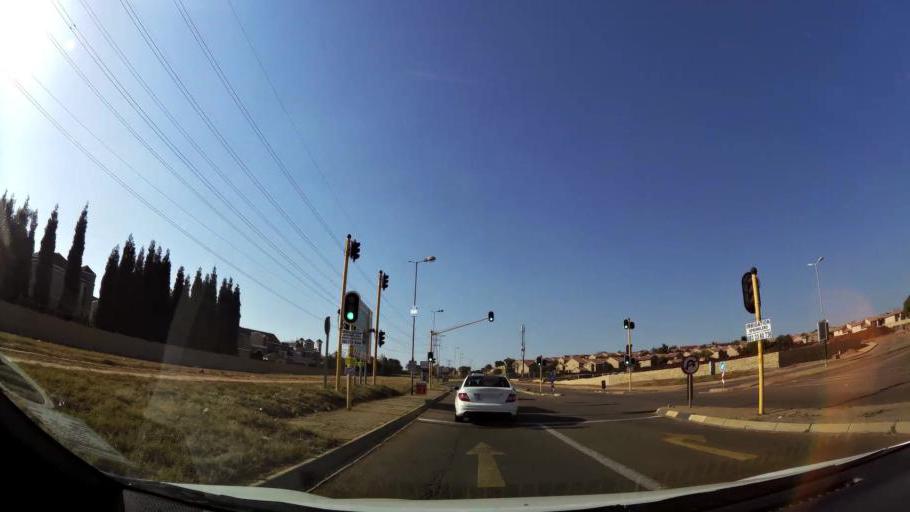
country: ZA
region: Gauteng
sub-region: City of Tshwane Metropolitan Municipality
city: Centurion
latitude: -25.8157
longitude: 28.3245
